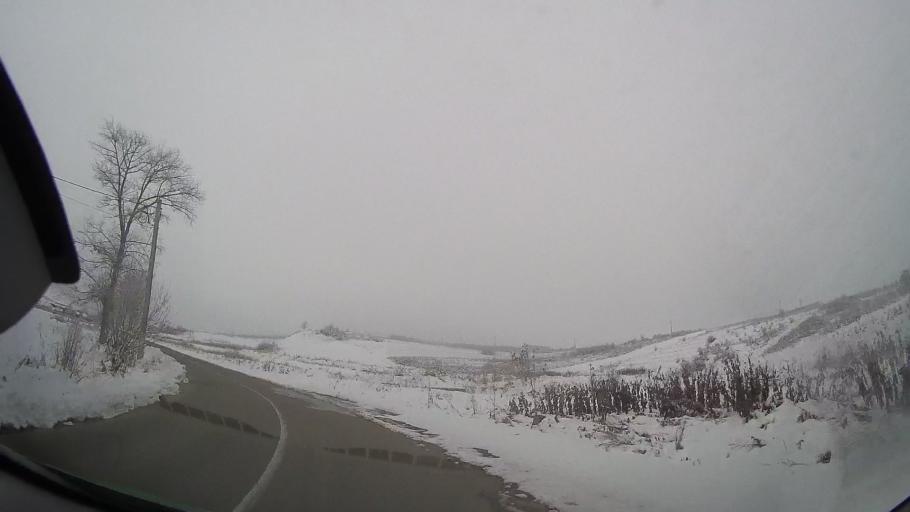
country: RO
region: Neamt
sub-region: Comuna Oniceni
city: Oniceni
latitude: 46.8004
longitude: 27.1246
